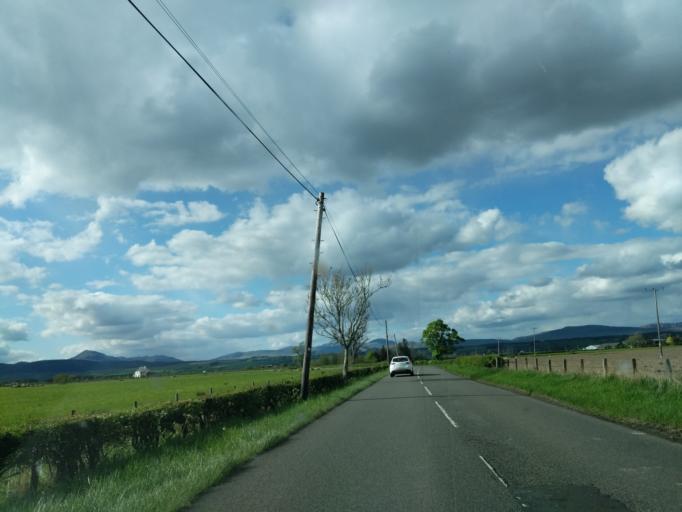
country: GB
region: Scotland
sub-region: Stirling
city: Doune
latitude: 56.1408
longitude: -4.1454
